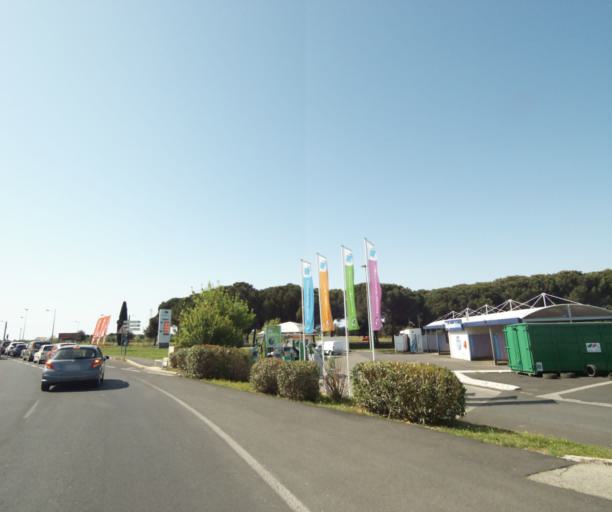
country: FR
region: Languedoc-Roussillon
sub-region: Departement de l'Herault
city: Perols
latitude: 43.5807
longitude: 3.9317
